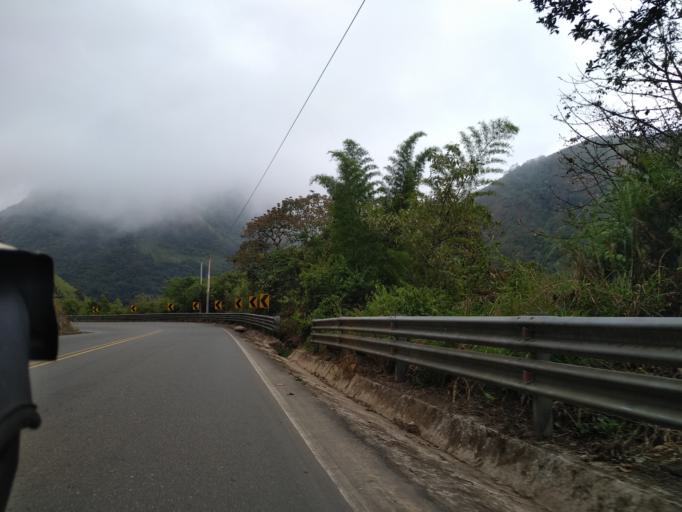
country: EC
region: Cotopaxi
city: La Mana
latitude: -0.8972
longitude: -79.0575
